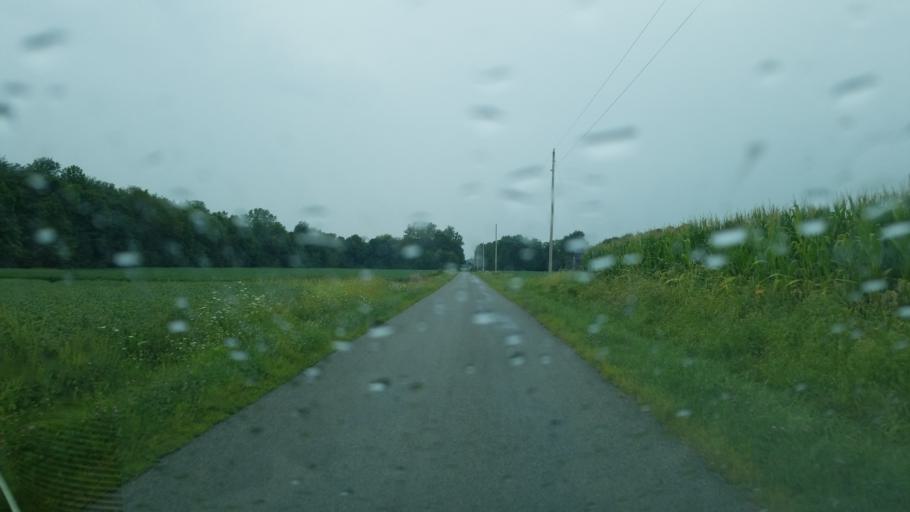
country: US
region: Ohio
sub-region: Richland County
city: Shelby
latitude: 40.9310
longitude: -82.7617
